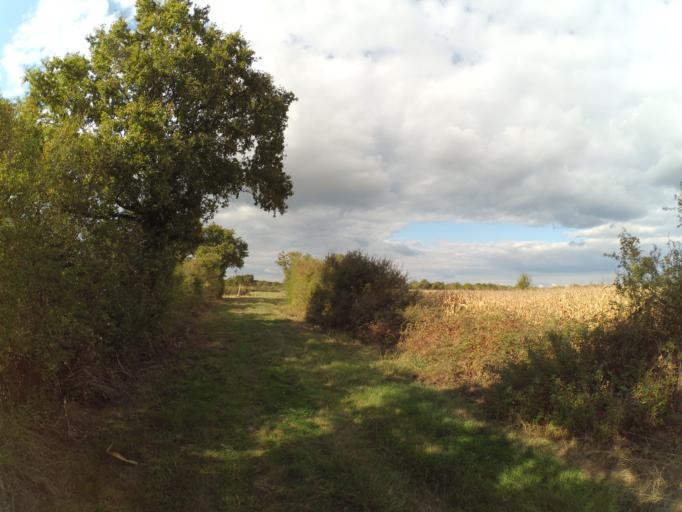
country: FR
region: Pays de la Loire
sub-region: Departement de la Loire-Atlantique
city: Saint-Lumine-de-Clisson
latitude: 47.0649
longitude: -1.3417
